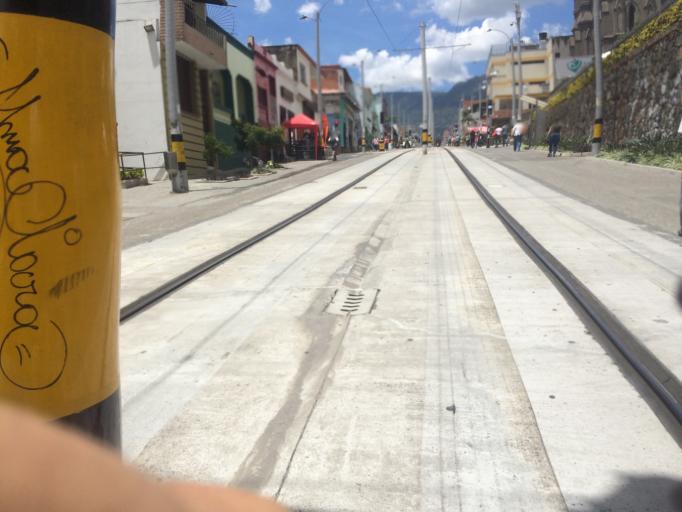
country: CO
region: Antioquia
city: Medellin
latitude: 6.2433
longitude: -75.5575
